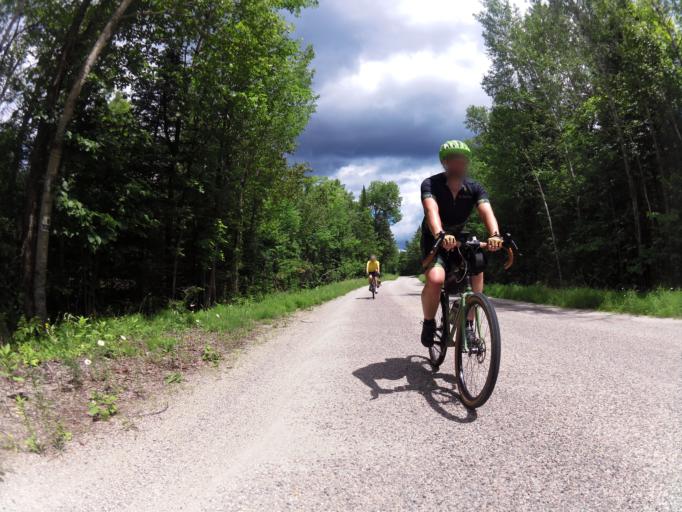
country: CA
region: Ontario
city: Renfrew
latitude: 45.0304
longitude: -76.7433
